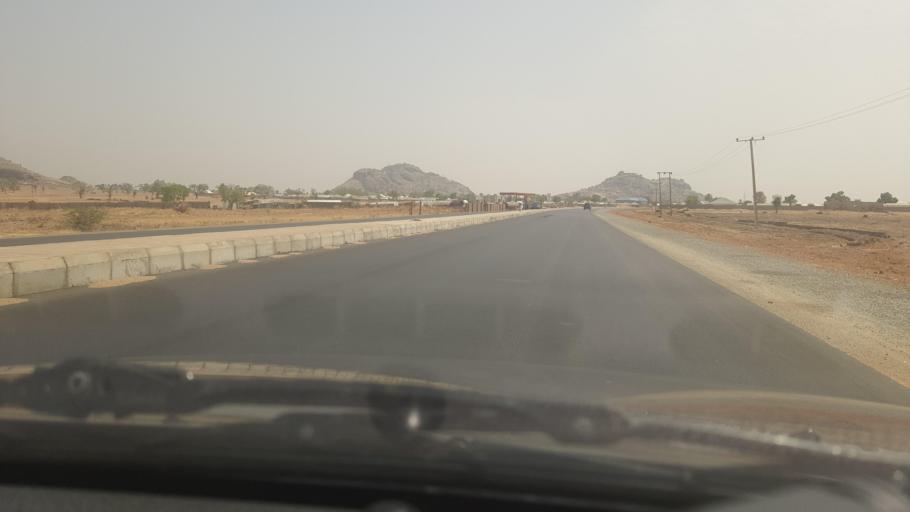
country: NG
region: Bauchi
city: Bauchi
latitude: 10.2986
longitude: 9.7365
